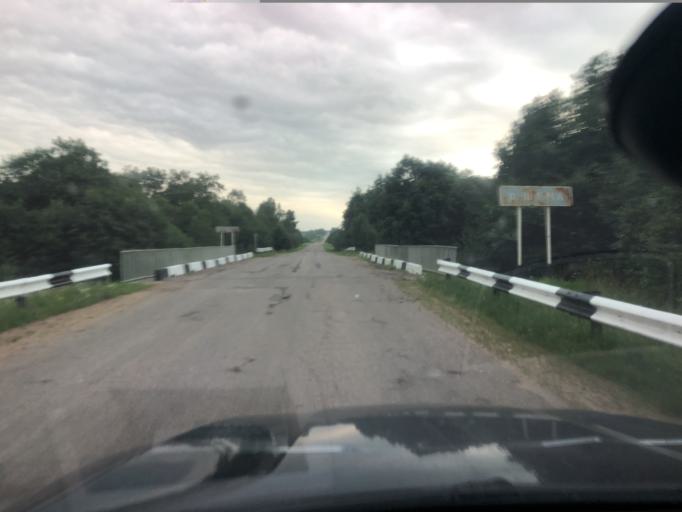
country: RU
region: Jaroslavl
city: Petrovsk
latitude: 57.0138
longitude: 38.9941
